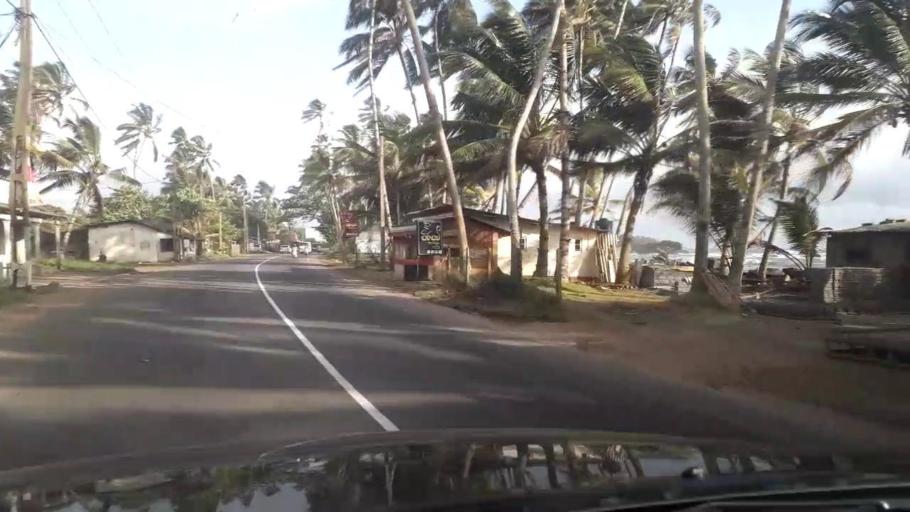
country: LK
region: Western
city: Beruwala
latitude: 6.5170
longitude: 79.9803
